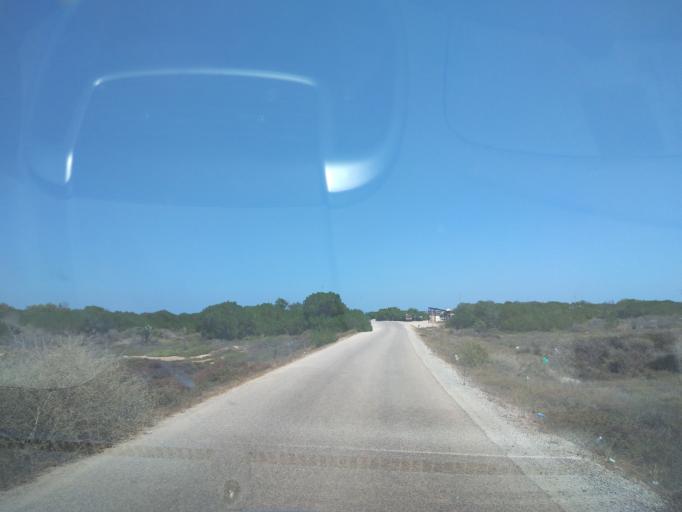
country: TN
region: Susah
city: Harqalah
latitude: 36.1330
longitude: 10.4646
